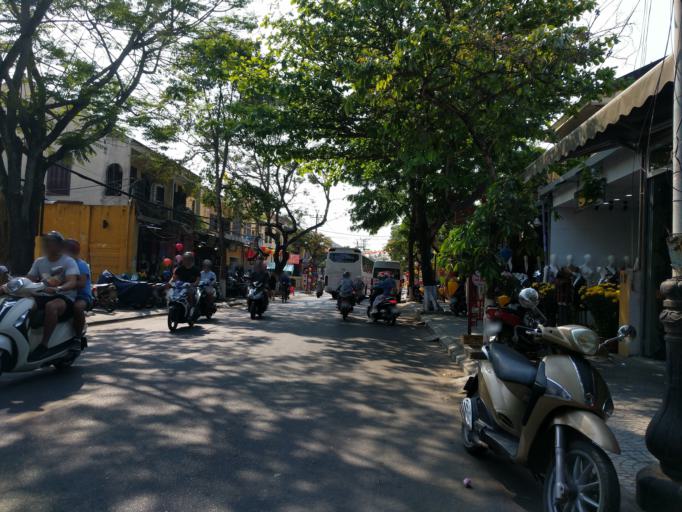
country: VN
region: Quang Nam
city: Hoi An
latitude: 15.8800
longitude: 108.3277
